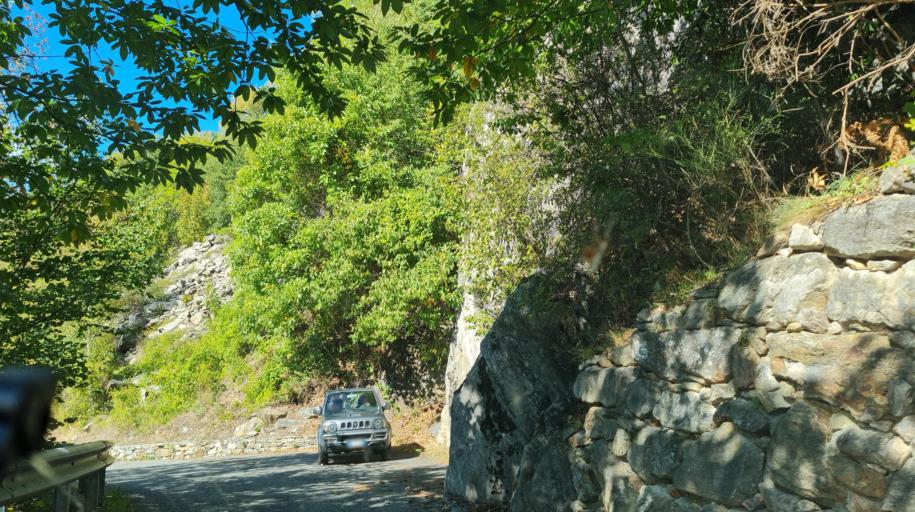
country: IT
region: Aosta Valley
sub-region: Valle d'Aosta
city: Arnad
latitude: 45.6444
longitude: 7.7495
